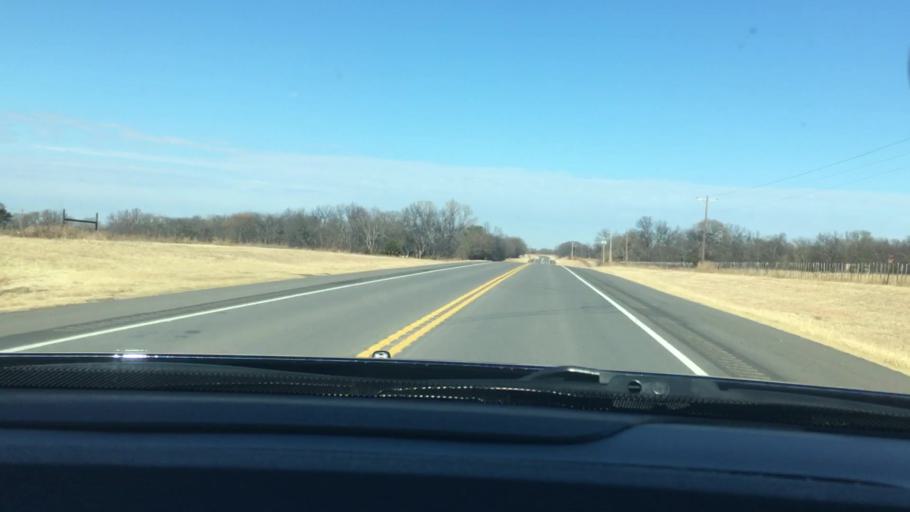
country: US
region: Oklahoma
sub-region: Murray County
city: Davis
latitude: 34.5551
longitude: -97.1335
